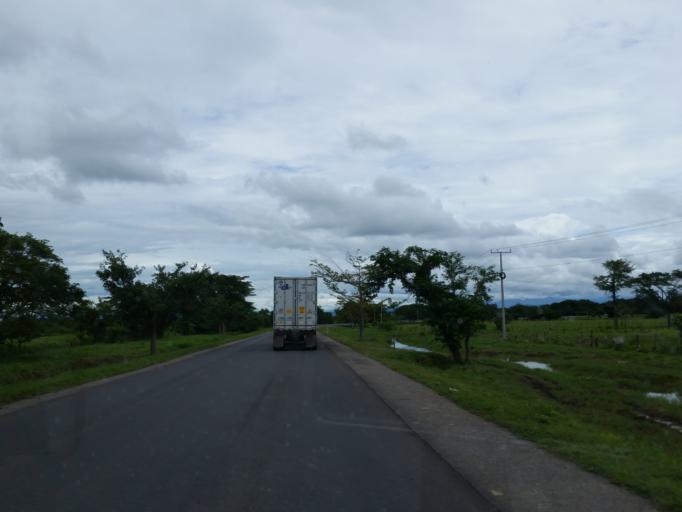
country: NI
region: Chinandega
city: Somotillo
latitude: 12.8580
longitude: -86.8692
